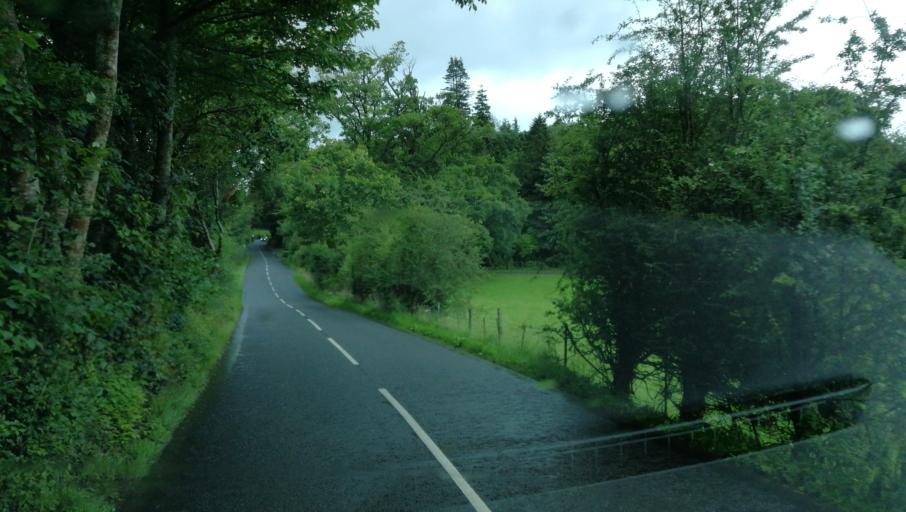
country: GB
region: England
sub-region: Cumbria
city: Penrith
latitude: 54.5851
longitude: -2.8688
